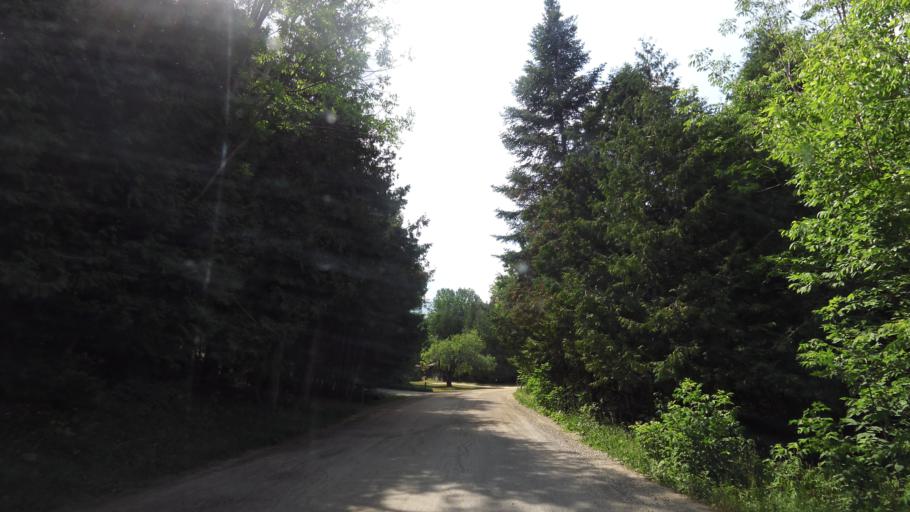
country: CA
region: Ontario
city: Orangeville
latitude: 43.9863
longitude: -80.0453
